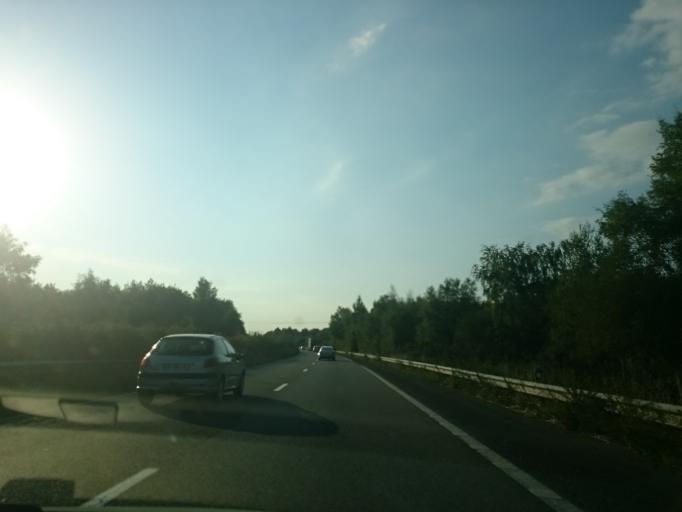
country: FR
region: Pays de la Loire
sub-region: Departement de la Loire-Atlantique
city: Missillac
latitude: 47.4698
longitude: -2.1631
